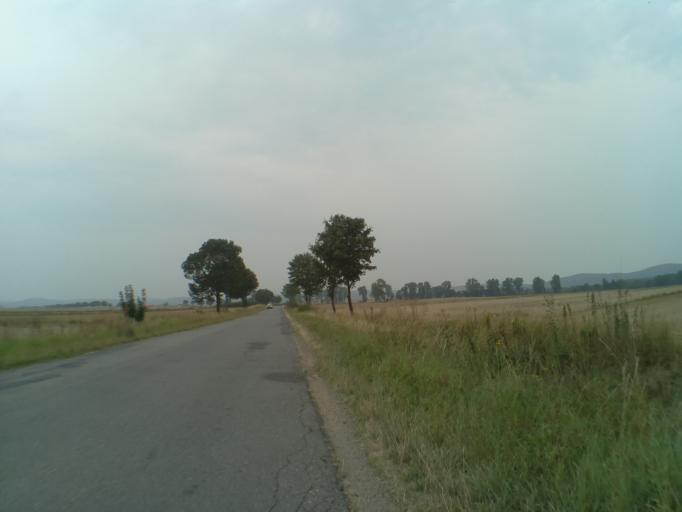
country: PL
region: Lower Silesian Voivodeship
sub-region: Powiat swidnicki
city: Swiebodzice
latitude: 50.8927
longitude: 16.3222
